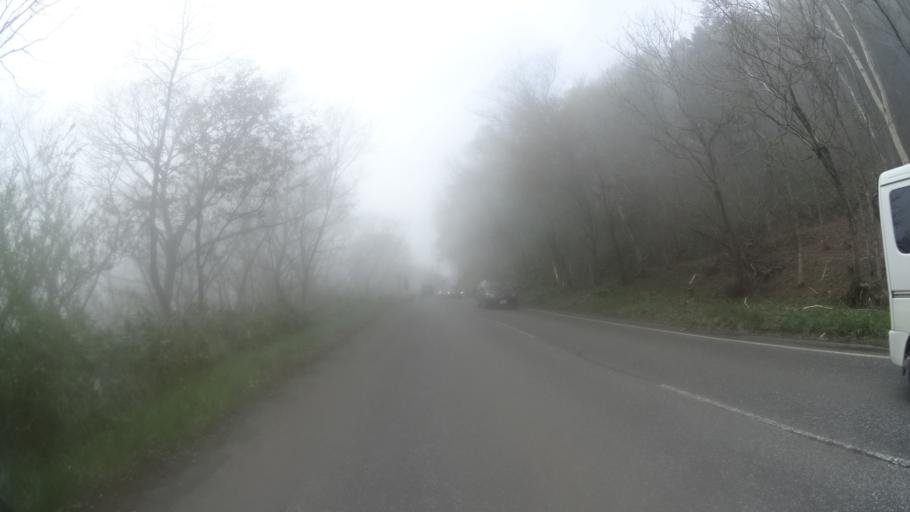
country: JP
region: Nagano
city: Nakano
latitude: 36.7201
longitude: 138.4775
